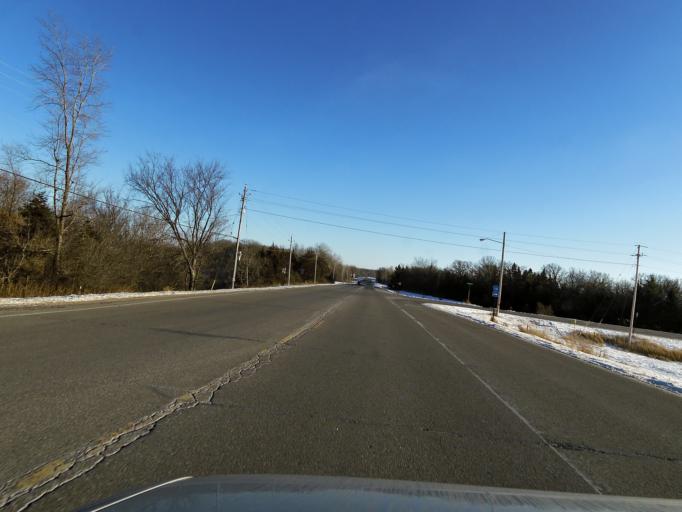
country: US
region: Minnesota
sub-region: Scott County
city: Shakopee
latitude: 44.7335
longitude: -93.4981
